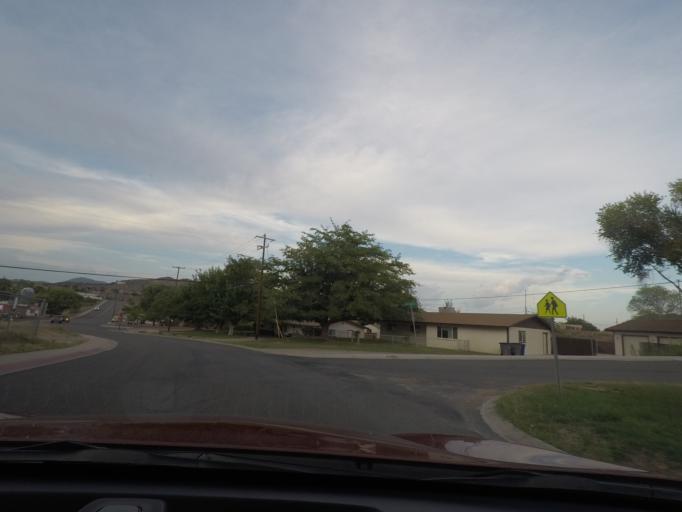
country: US
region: Arizona
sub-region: Yavapai County
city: Bagdad
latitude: 34.5716
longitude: -113.1793
